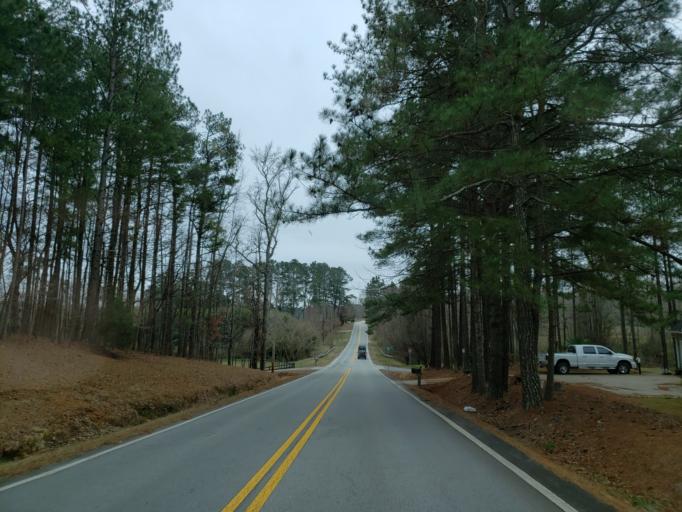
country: US
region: Georgia
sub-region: Paulding County
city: Hiram
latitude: 33.9141
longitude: -84.7239
